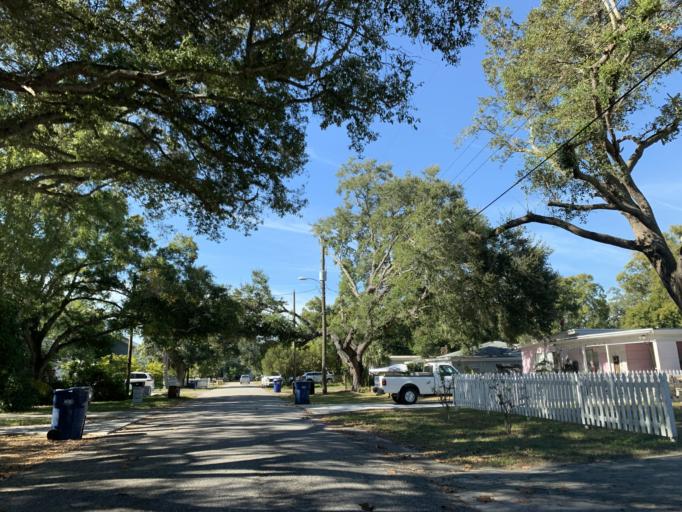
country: US
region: Florida
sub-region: Hillsborough County
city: Tampa
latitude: 27.8908
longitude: -82.5034
